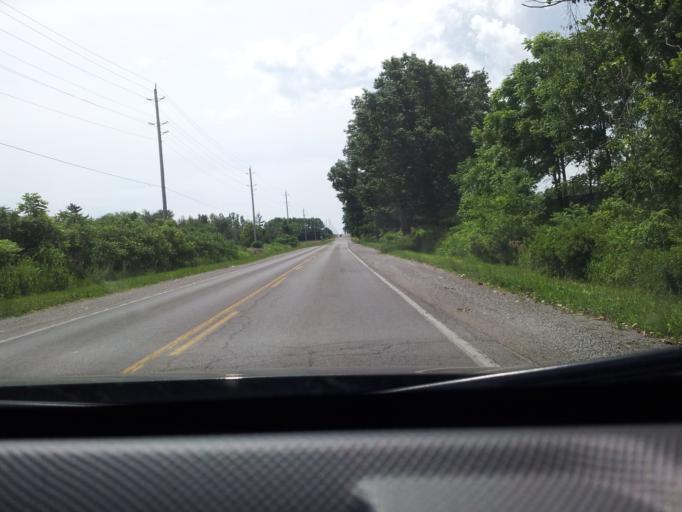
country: CA
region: Ontario
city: Norfolk County
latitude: 42.8053
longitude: -80.2460
